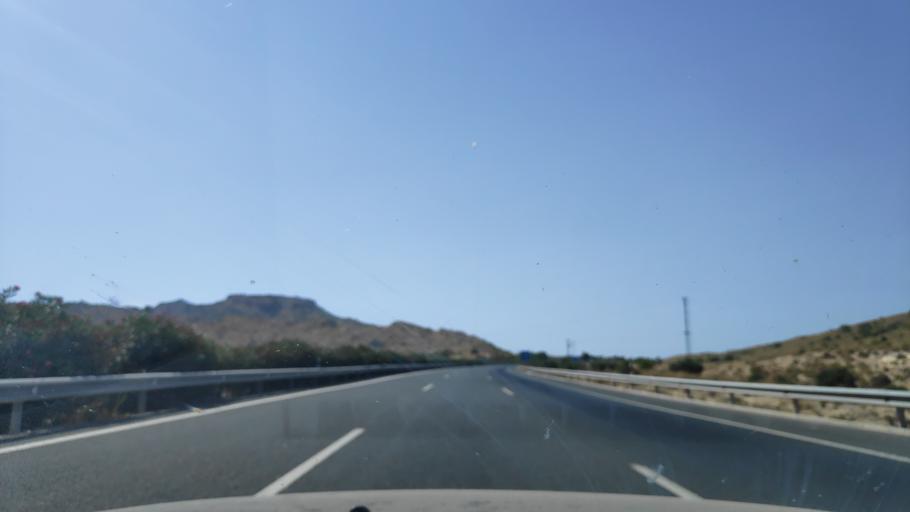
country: ES
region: Murcia
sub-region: Murcia
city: Ulea
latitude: 38.1660
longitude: -1.3057
